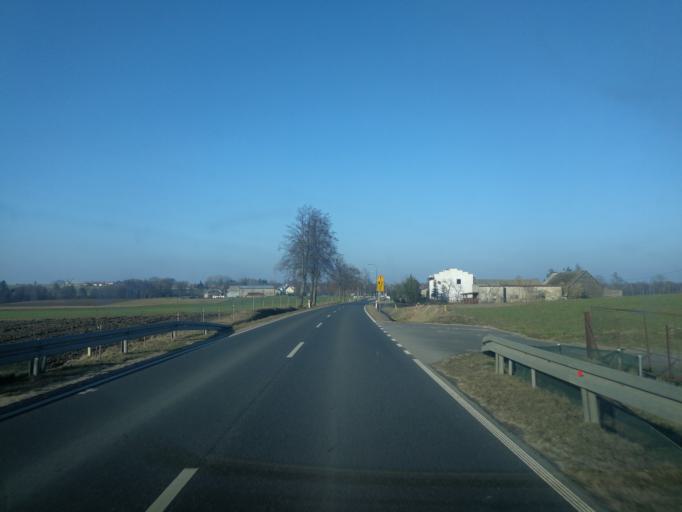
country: PL
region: Warmian-Masurian Voivodeship
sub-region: Powiat ilawski
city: Lubawa
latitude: 53.4510
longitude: 19.7778
